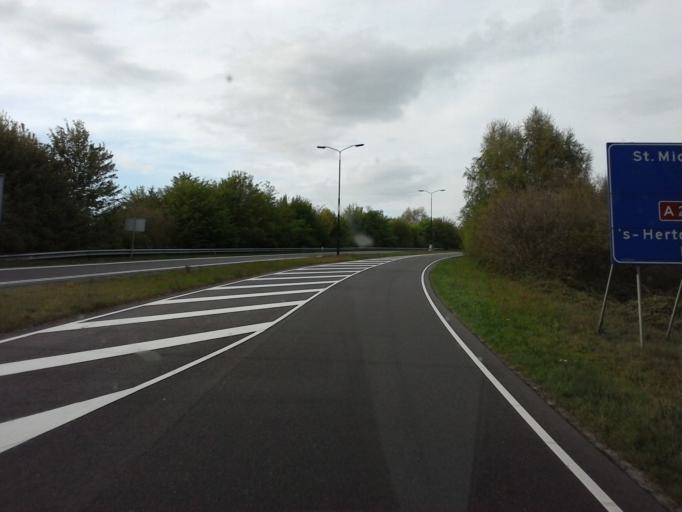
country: NL
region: North Brabant
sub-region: Gemeente Boxtel
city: Boxtel
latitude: 51.6140
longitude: 5.3166
